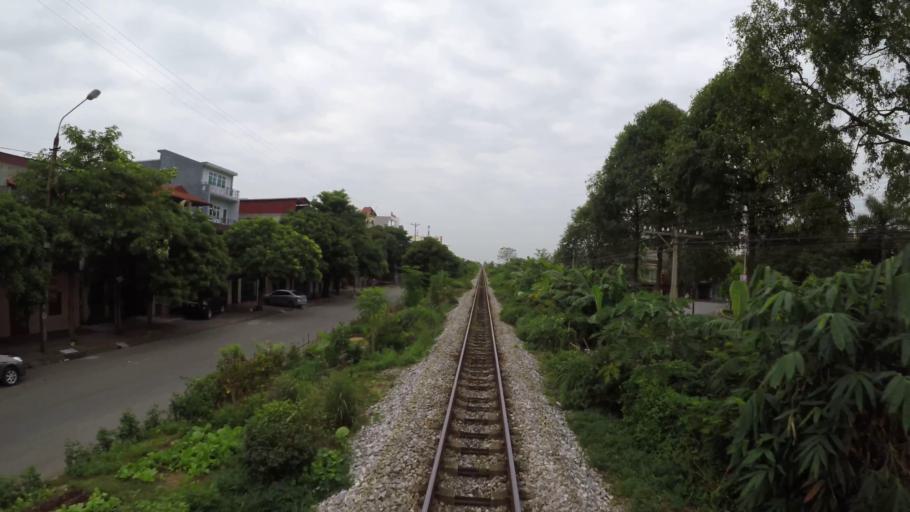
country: VN
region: Hai Duong
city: Thanh Pho Hai Duong
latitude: 20.9435
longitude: 106.3562
